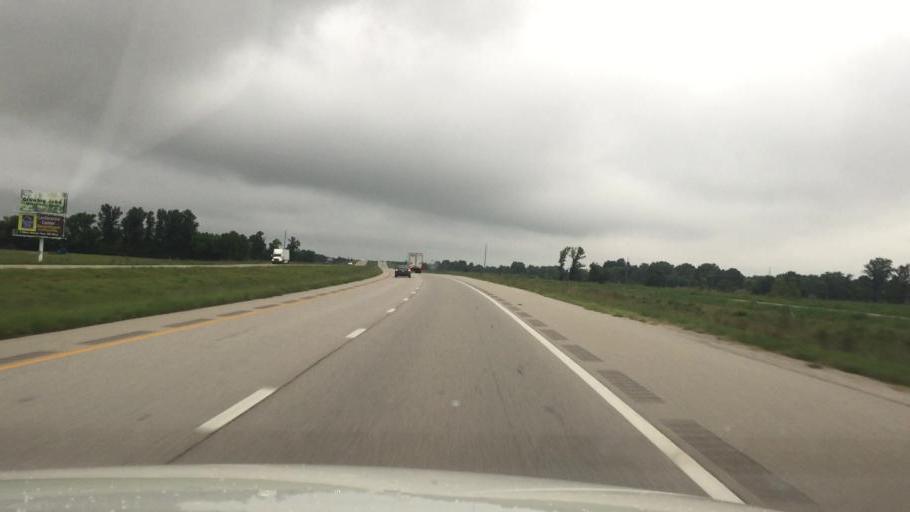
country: US
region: Kansas
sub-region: Montgomery County
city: Coffeyville
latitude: 37.1001
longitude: -95.5896
